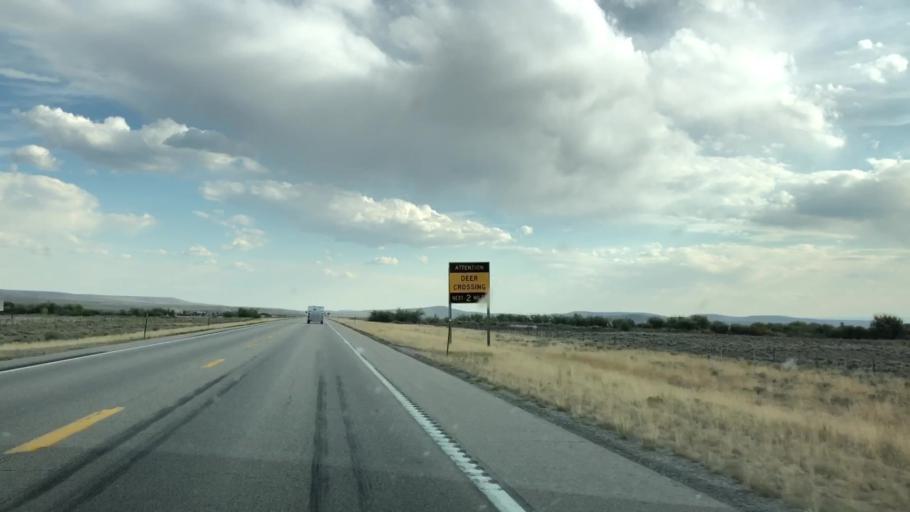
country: US
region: Wyoming
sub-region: Sublette County
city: Pinedale
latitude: 42.9803
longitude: -110.0915
